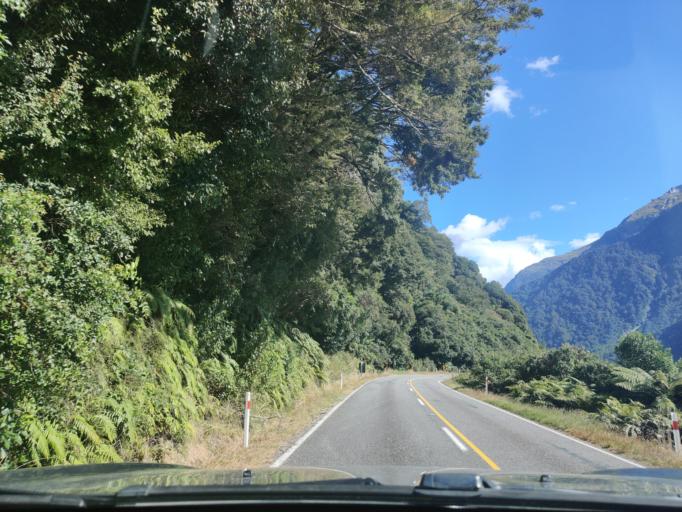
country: NZ
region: Otago
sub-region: Queenstown-Lakes District
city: Wanaka
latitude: -43.9725
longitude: 169.4193
